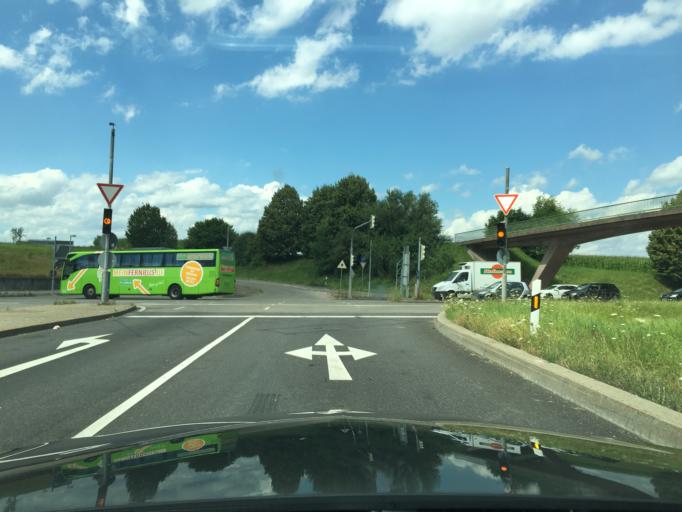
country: DE
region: Baden-Wuerttemberg
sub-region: Regierungsbezirk Stuttgart
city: Filderstadt
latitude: 48.6947
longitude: 9.2219
